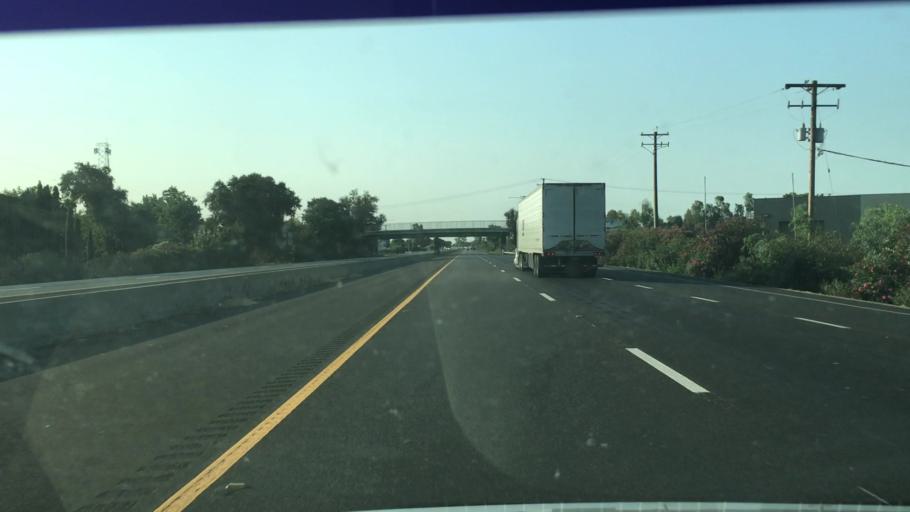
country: US
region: California
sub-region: San Joaquin County
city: Collierville
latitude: 38.2201
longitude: -121.2719
